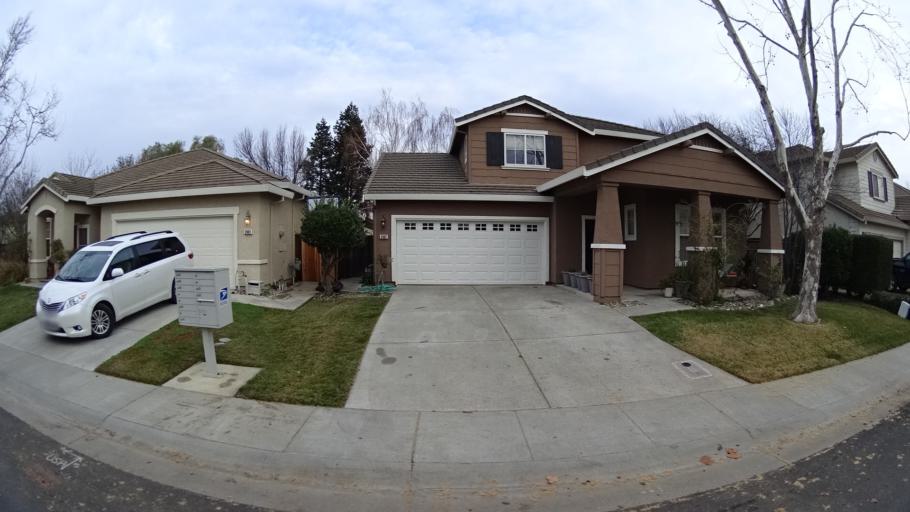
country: US
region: California
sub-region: Yolo County
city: Davis
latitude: 38.5668
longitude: -121.7242
